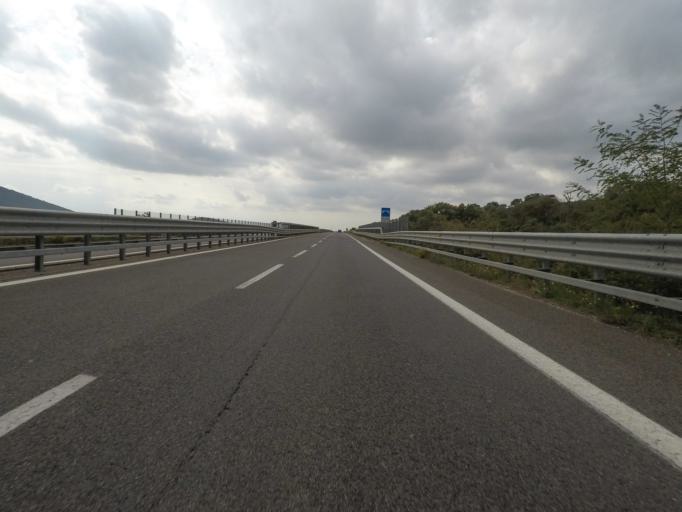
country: IT
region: Tuscany
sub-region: Provincia di Grosseto
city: Bagno Roselle
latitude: 42.8354
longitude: 11.1470
